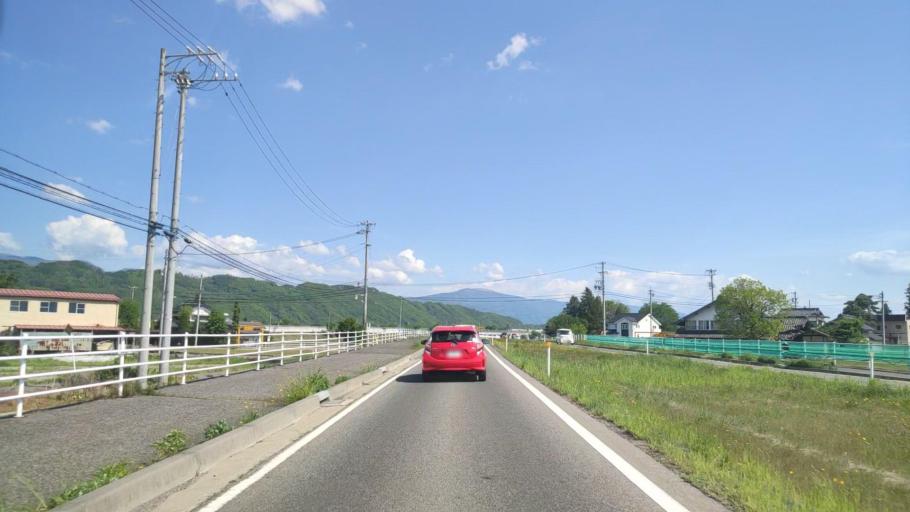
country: JP
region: Nagano
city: Toyoshina
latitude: 36.2762
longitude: 137.9268
